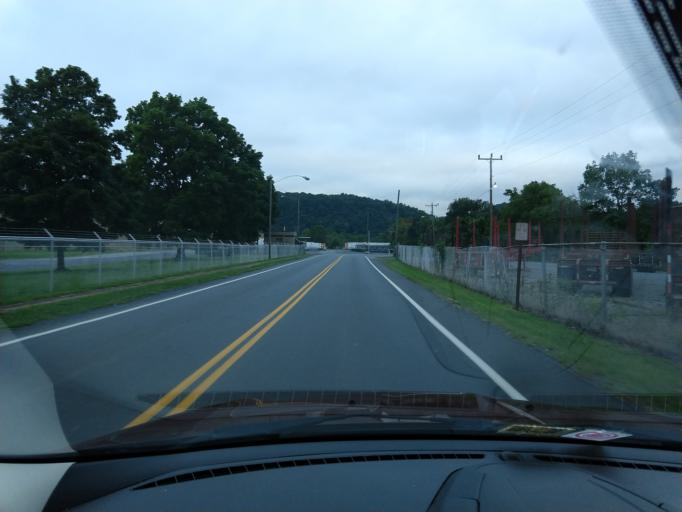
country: US
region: Virginia
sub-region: City of Covington
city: Fairlawn
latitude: 37.7607
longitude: -79.9996
